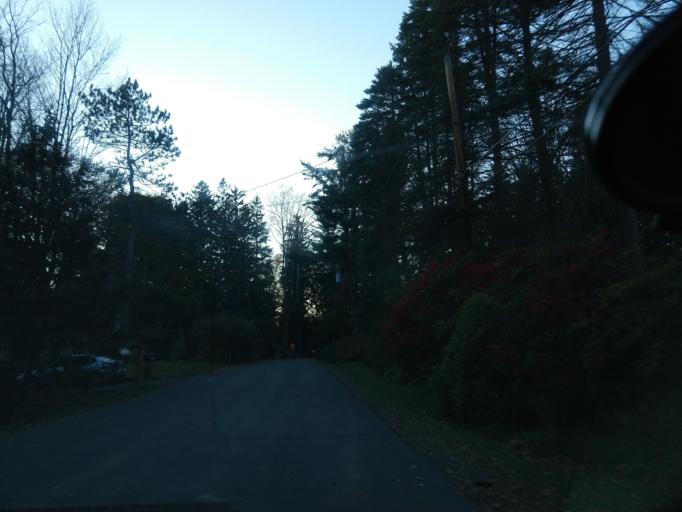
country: US
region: New York
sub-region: Tompkins County
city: Northeast Ithaca
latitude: 42.4656
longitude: -76.4710
